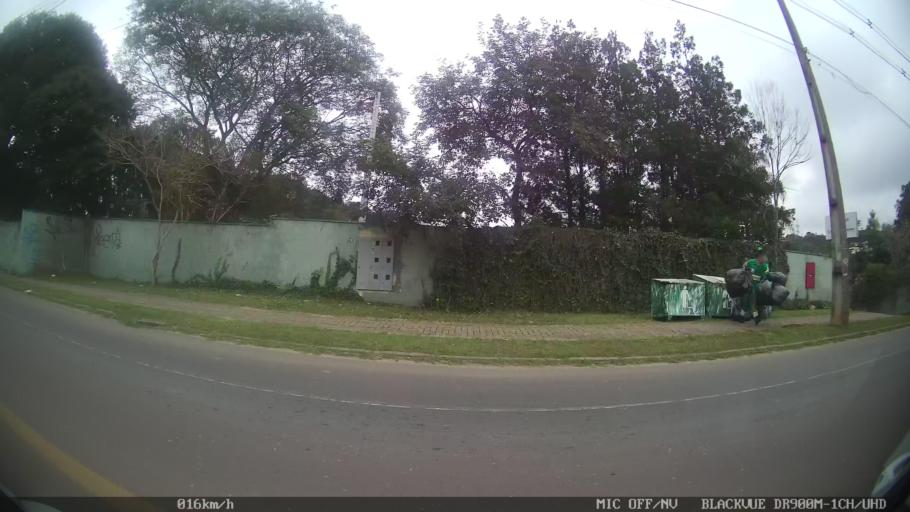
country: BR
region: Parana
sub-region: Curitiba
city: Curitiba
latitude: -25.3699
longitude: -49.2733
